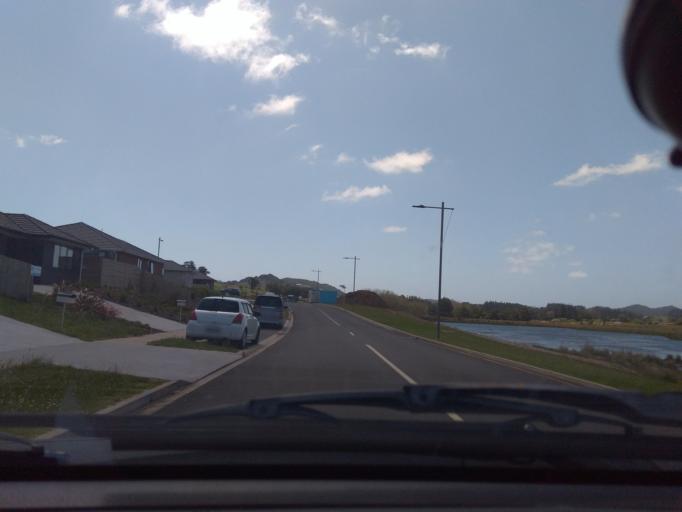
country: NZ
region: Northland
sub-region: Whangarei
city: Whangarei
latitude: -35.6763
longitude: 174.3194
